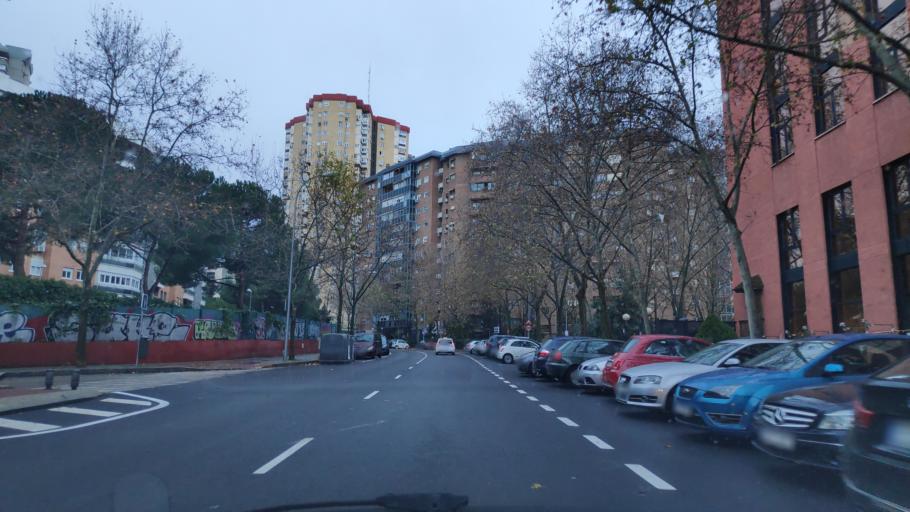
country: ES
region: Madrid
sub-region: Provincia de Madrid
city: Pinar de Chamartin
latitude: 40.4824
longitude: -3.6703
